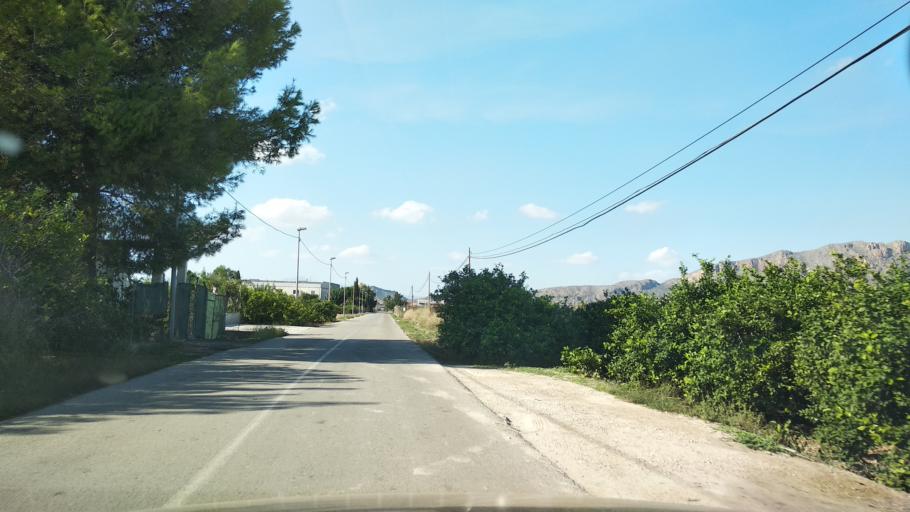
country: ES
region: Murcia
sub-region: Murcia
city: Santomera
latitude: 38.0494
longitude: -1.0397
